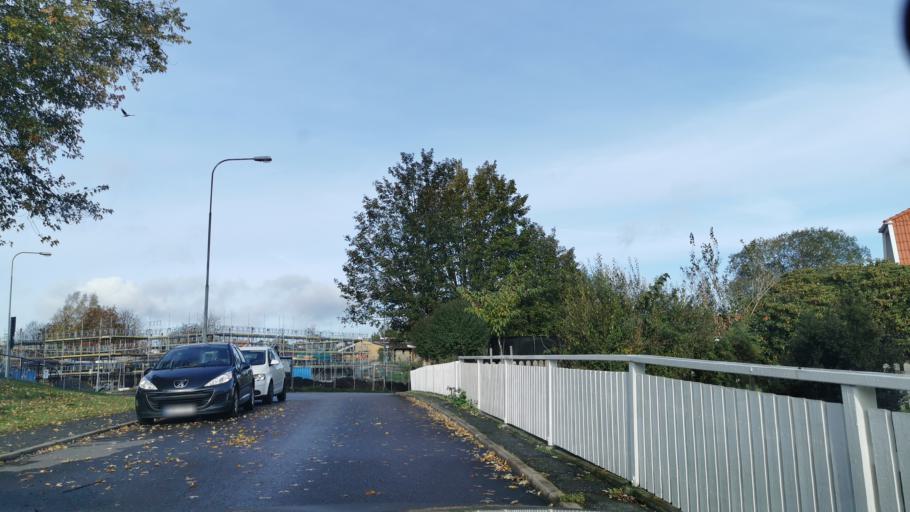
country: SE
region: Vaestra Goetaland
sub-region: Partille Kommun
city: Partille
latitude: 57.7291
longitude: 12.0874
